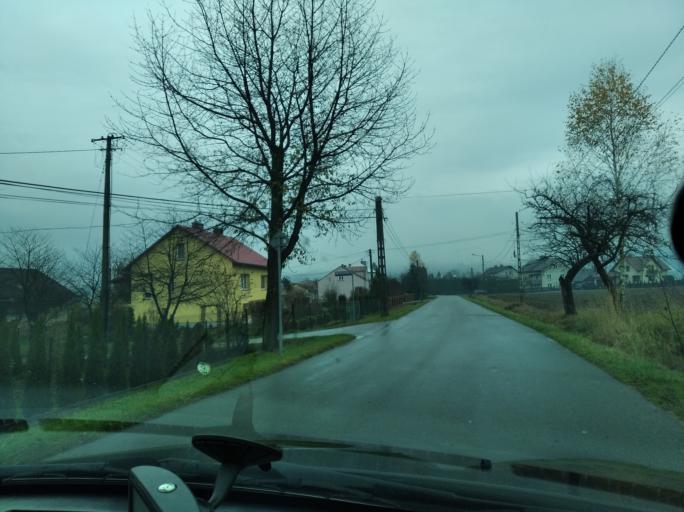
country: PL
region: Subcarpathian Voivodeship
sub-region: Powiat strzyzowski
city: Babica
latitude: 49.9260
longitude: 21.8571
